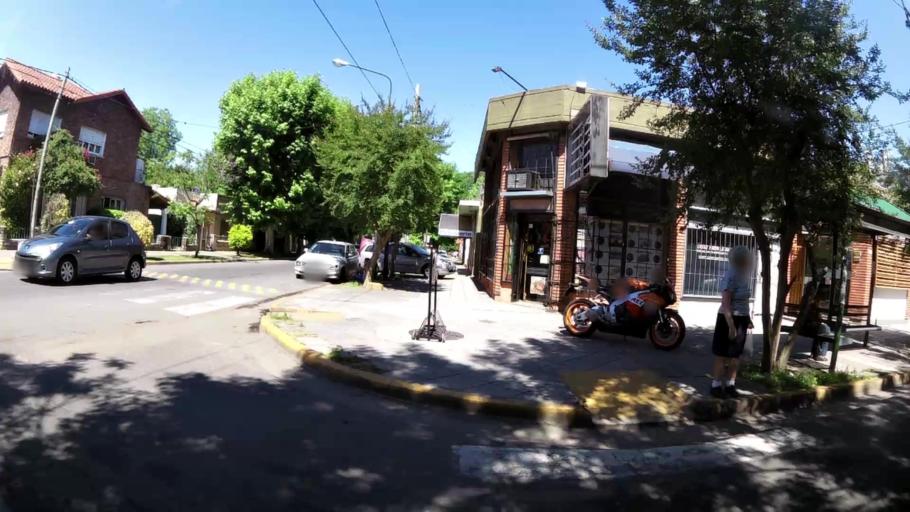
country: AR
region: Buenos Aires
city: Ituzaingo
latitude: -34.6601
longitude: -58.6640
